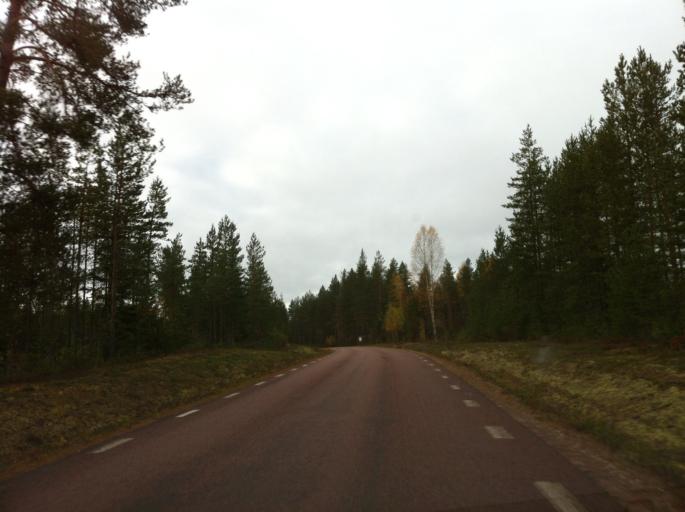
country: SE
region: Dalarna
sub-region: Mora Kommun
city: Mora
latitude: 61.1100
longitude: 14.4615
